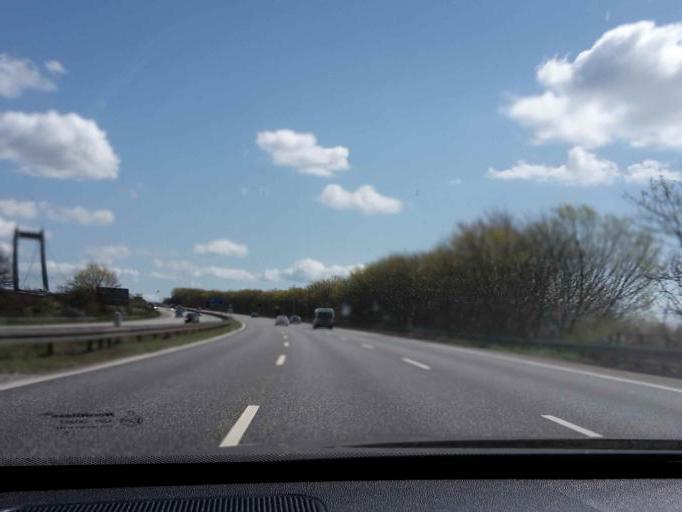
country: DK
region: South Denmark
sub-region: Fredericia Kommune
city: Snoghoj
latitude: 55.5237
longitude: 9.7299
